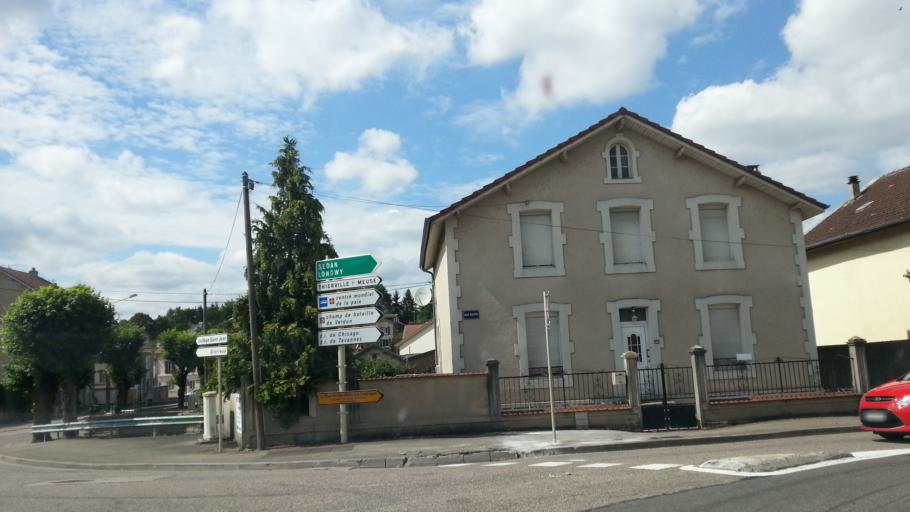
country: FR
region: Lorraine
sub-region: Departement de la Meuse
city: Thierville-sur-Meuse
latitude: 49.1577
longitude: 5.3647
